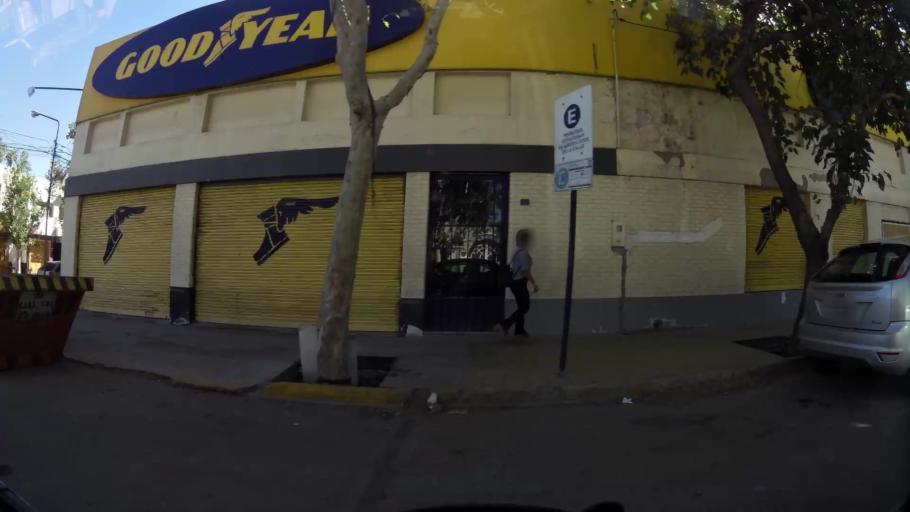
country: AR
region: San Juan
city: San Juan
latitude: -31.5370
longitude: -68.5350
